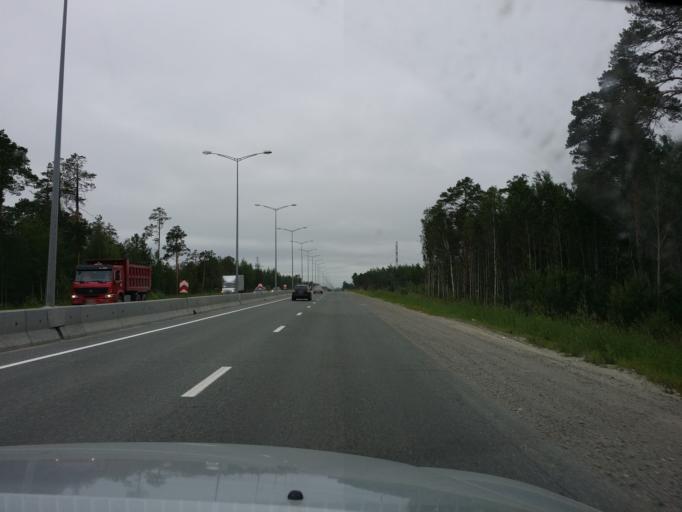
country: RU
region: Khanty-Mansiyskiy Avtonomnyy Okrug
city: Nizhnevartovsk
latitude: 60.9963
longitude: 76.4275
